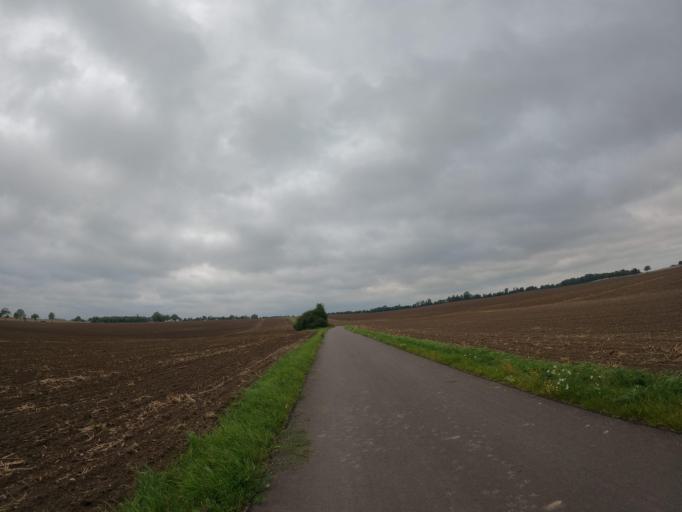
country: DE
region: Mecklenburg-Vorpommern
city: Rambin
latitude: 54.3156
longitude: 13.1813
